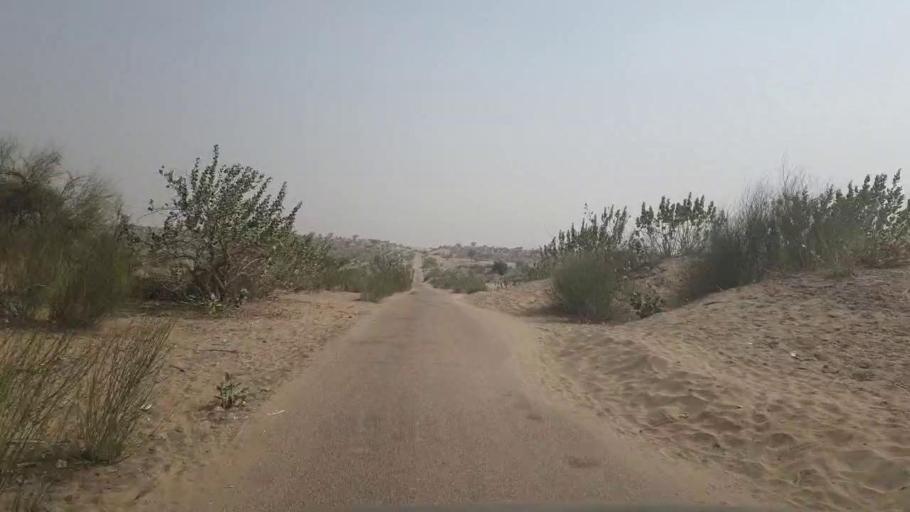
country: PK
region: Sindh
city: Chor
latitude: 25.5959
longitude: 70.0025
